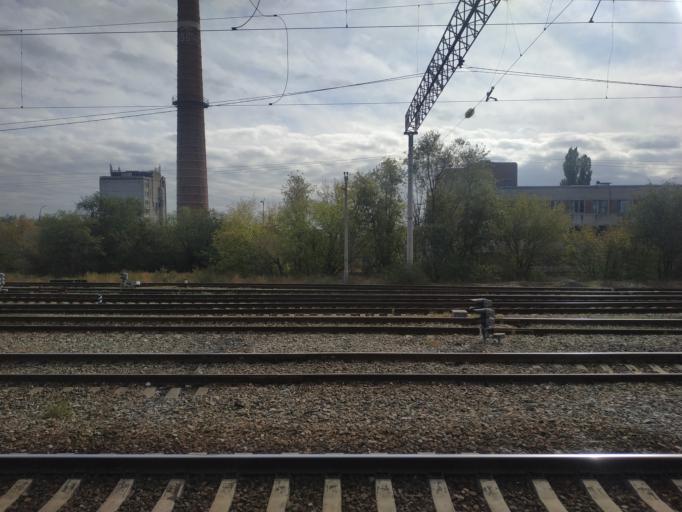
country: RU
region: Volgograd
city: Volgograd
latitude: 48.6675
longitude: 44.4595
